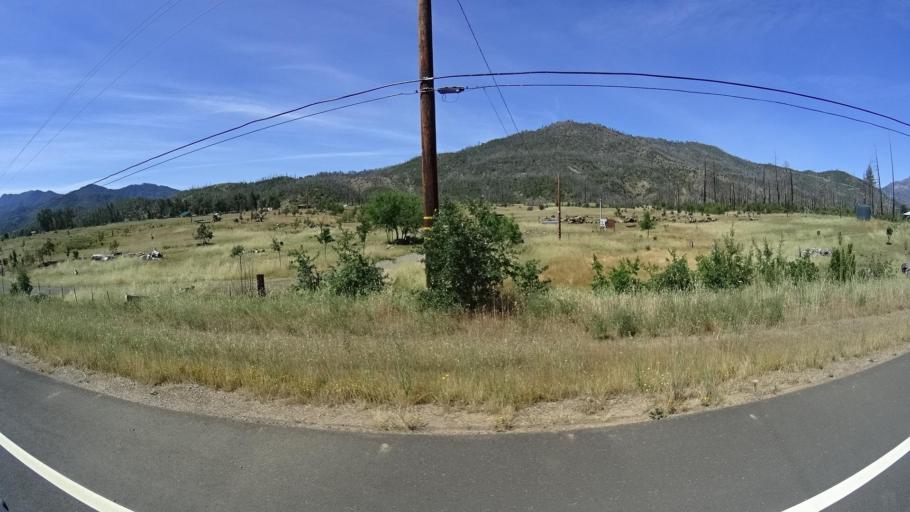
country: US
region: California
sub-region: Lake County
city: Middletown
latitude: 38.7600
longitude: -122.6417
